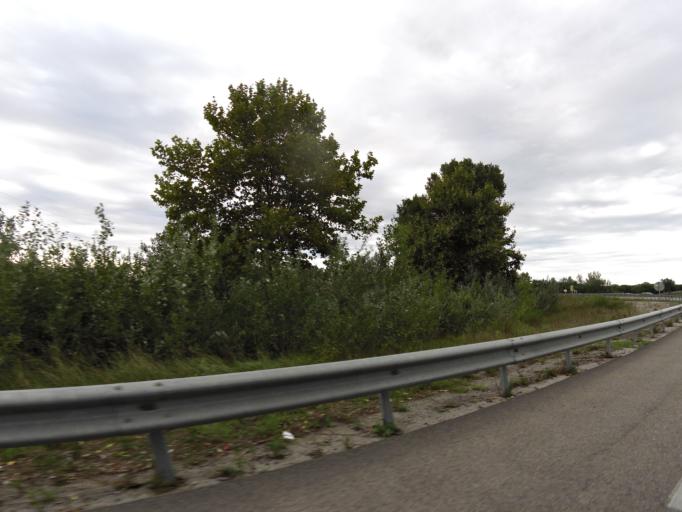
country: FR
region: Languedoc-Roussillon
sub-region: Departement du Gard
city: Aigues-Mortes
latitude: 43.5787
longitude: 4.2008
